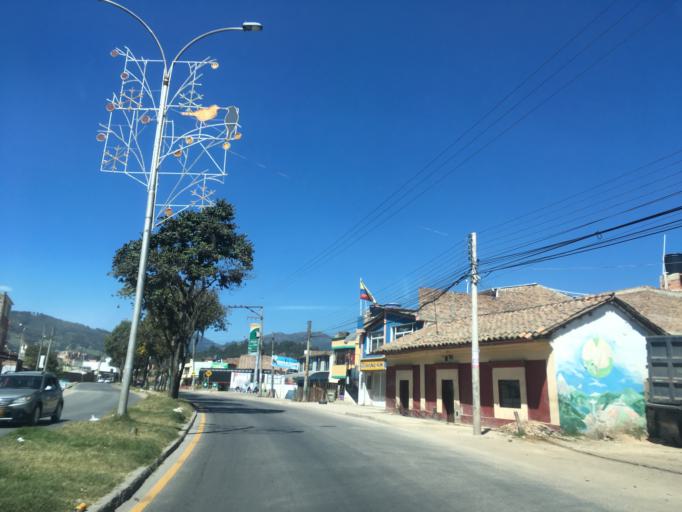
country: CO
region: Boyaca
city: Duitama
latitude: 5.8166
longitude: -73.0199
